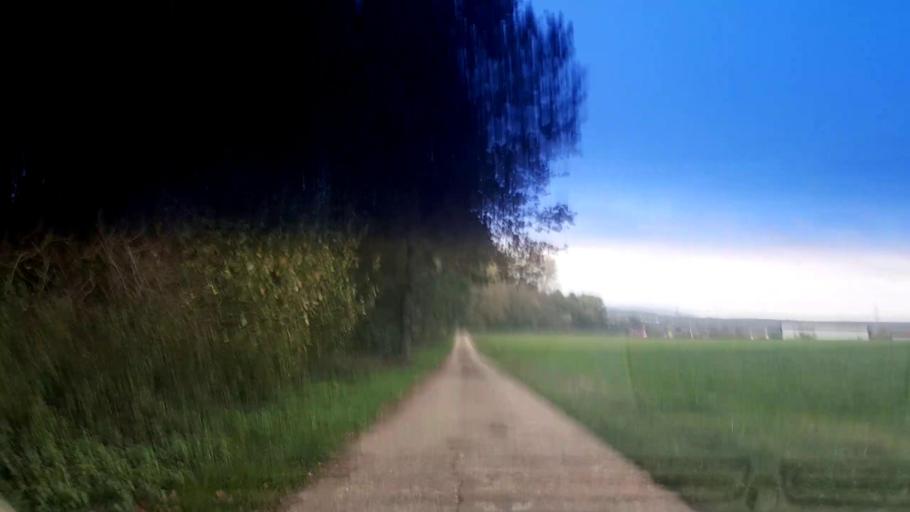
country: DE
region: Bavaria
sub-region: Upper Franconia
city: Memmelsdorf
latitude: 49.9656
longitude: 10.9577
